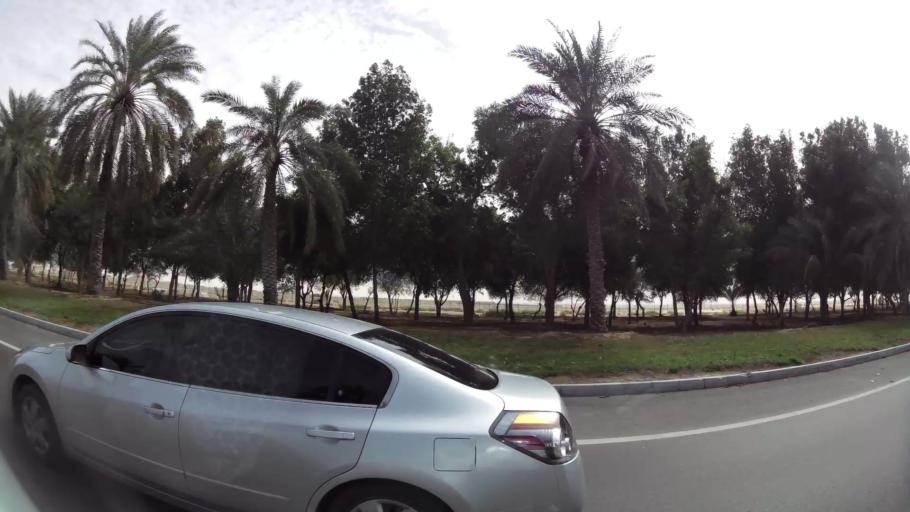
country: AE
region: Abu Dhabi
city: Abu Dhabi
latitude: 24.3954
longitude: 54.5643
